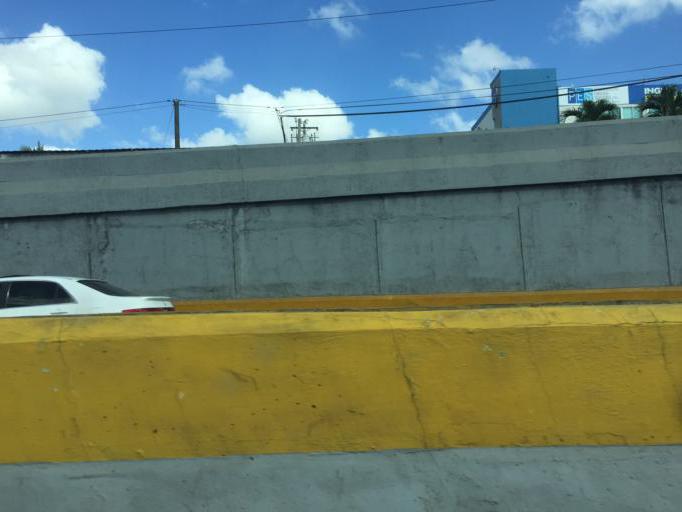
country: DO
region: Santo Domingo
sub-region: Santo Domingo
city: Santo Domingo Este
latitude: 18.4856
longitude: -69.8736
